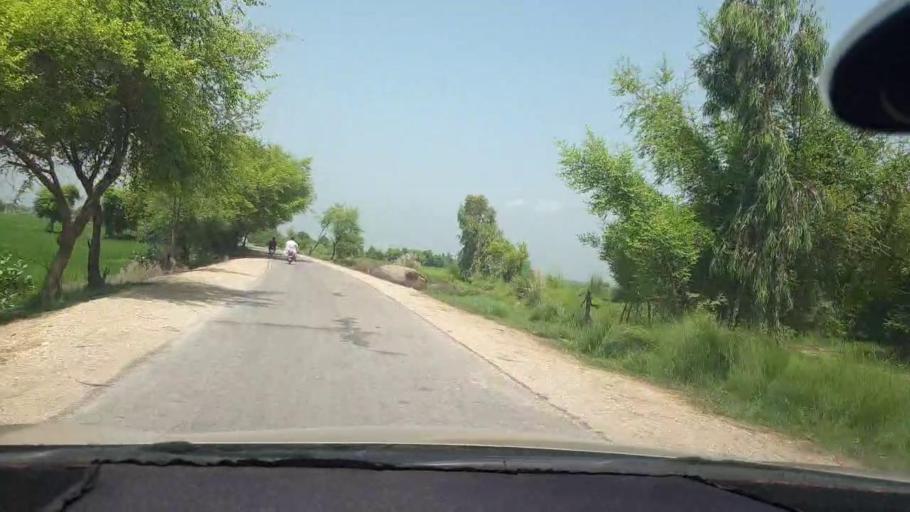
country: PK
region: Sindh
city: Kambar
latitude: 27.6433
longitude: 67.9729
